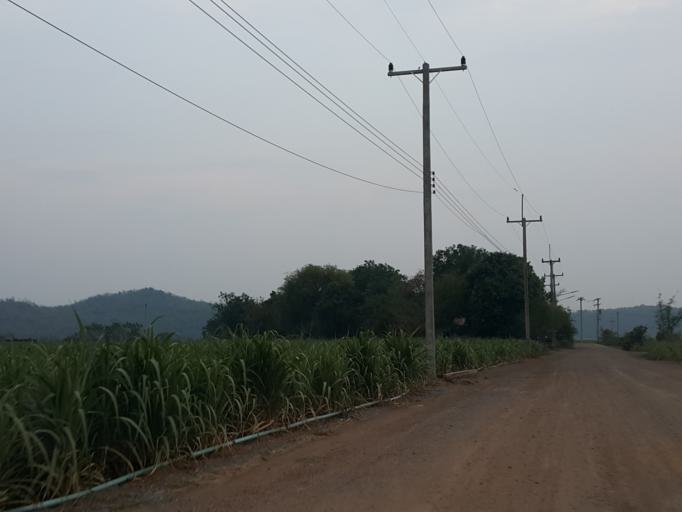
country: TH
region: Suphan Buri
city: Dan Chang
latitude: 14.9327
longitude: 99.6413
